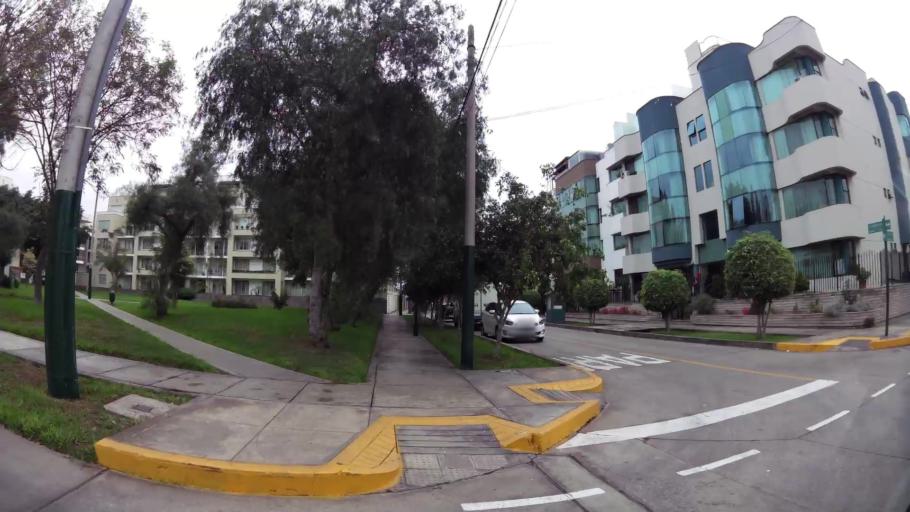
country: PE
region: Lima
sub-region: Lima
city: Surco
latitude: -12.1325
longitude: -77.0056
